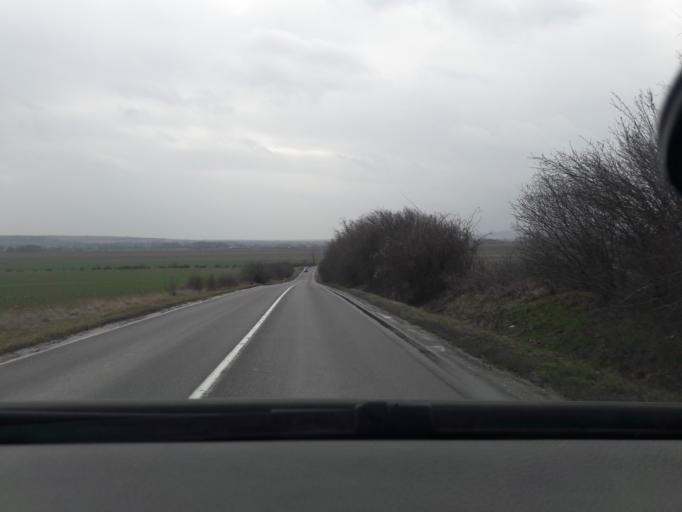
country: SK
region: Trnavsky
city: Smolenice
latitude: 48.4319
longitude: 17.4217
